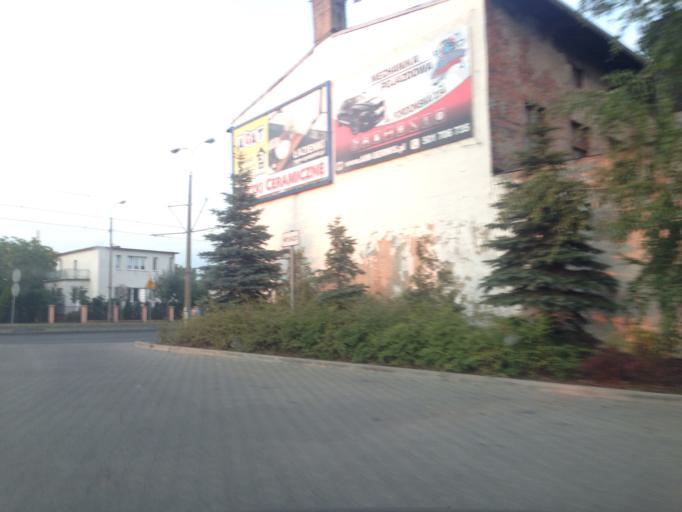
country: PL
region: Kujawsko-Pomorskie
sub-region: Bydgoszcz
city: Bydgoszcz
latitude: 53.1205
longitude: 18.0452
